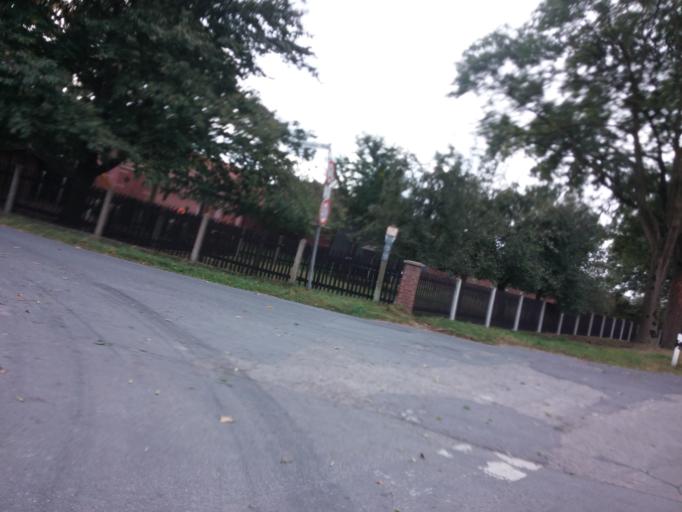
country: DE
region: North Rhine-Westphalia
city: Dorsten
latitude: 51.6398
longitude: 7.0165
